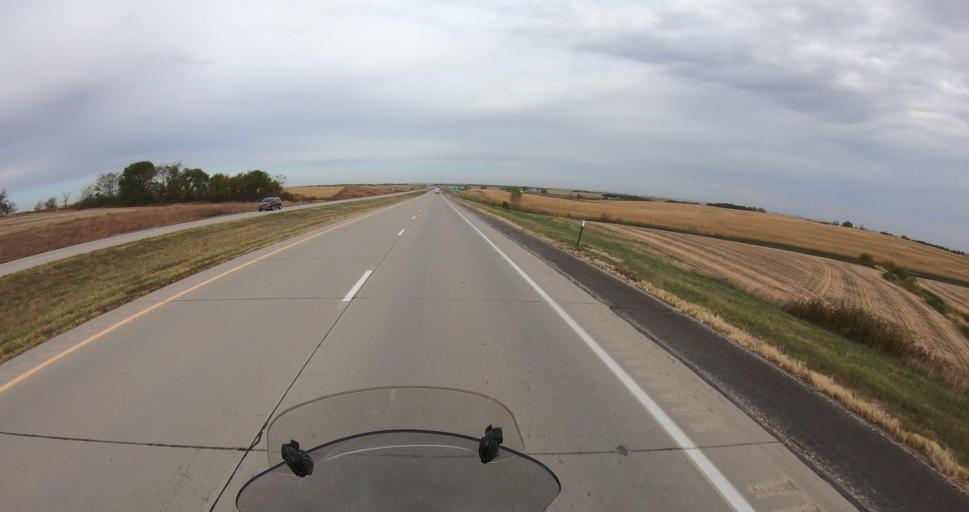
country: US
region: Nebraska
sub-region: Saunders County
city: Wahoo
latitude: 41.1425
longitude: -96.6317
